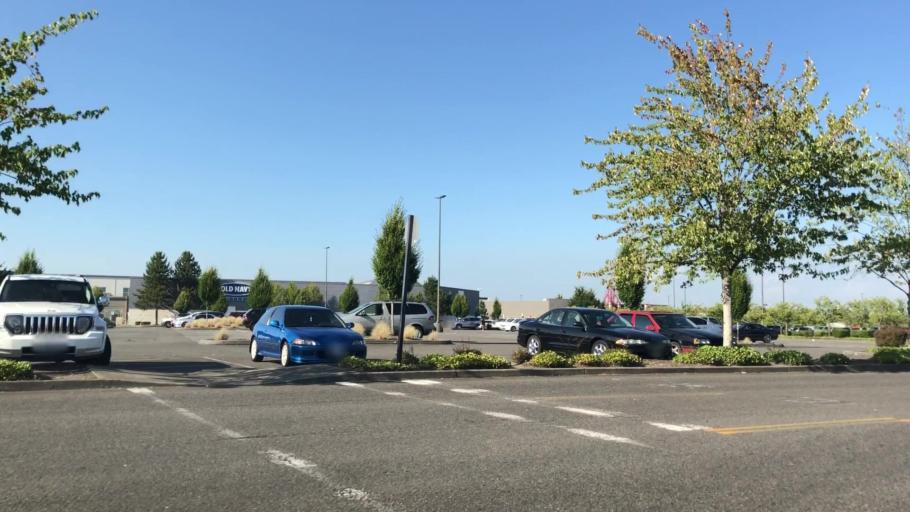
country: US
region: Washington
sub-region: King County
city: Algona
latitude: 47.2963
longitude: -122.2450
